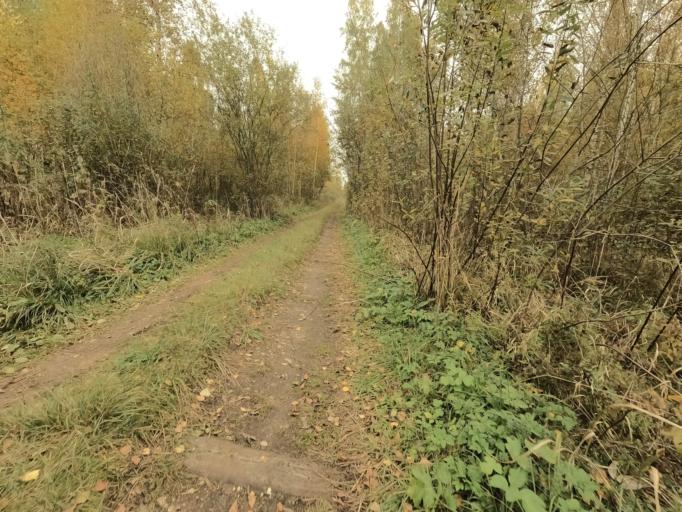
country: RU
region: Novgorod
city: Pankovka
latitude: 58.8730
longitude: 30.9382
